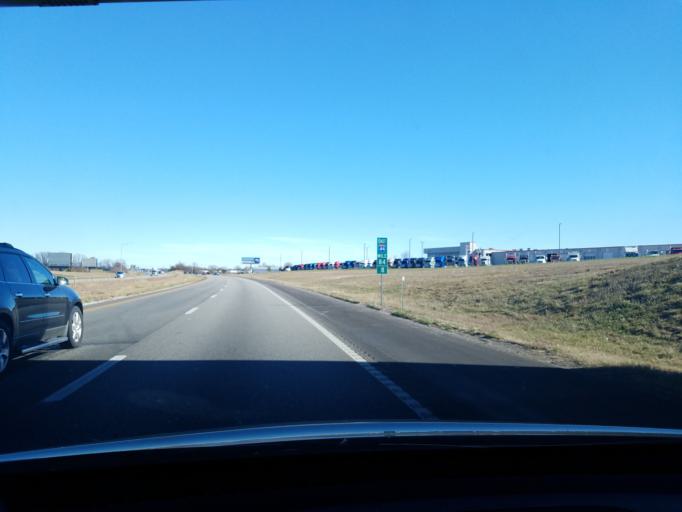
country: US
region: Missouri
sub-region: Greene County
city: Strafford
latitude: 37.2505
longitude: -93.1832
